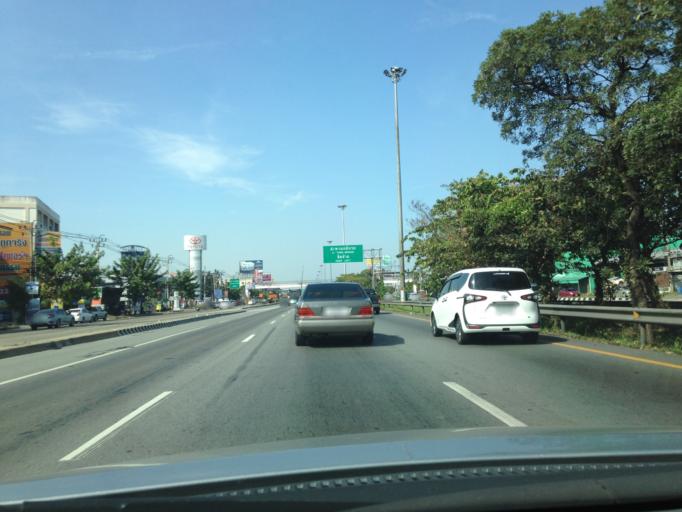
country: TH
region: Nonthaburi
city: Bang Yai
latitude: 13.8422
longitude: 100.4131
